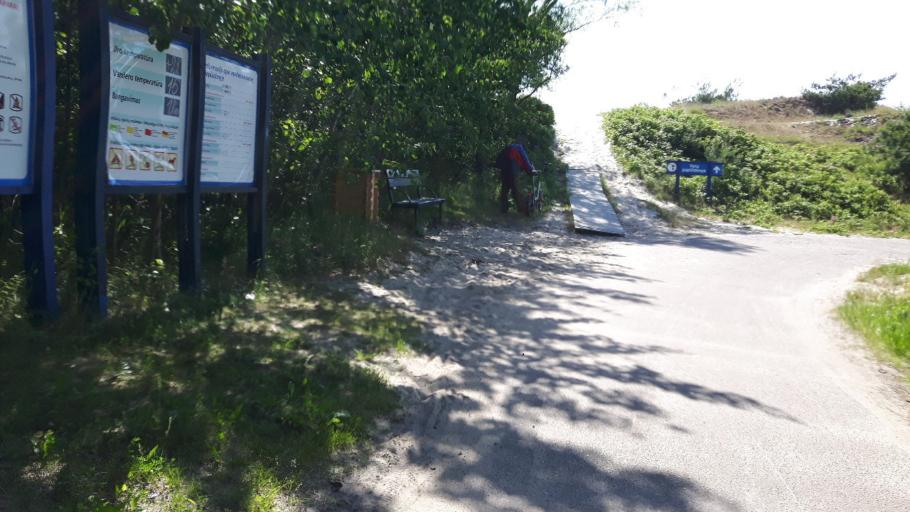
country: LT
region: Klaipedos apskritis
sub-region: Klaipeda
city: Klaipeda
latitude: 55.6941
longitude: 21.1026
